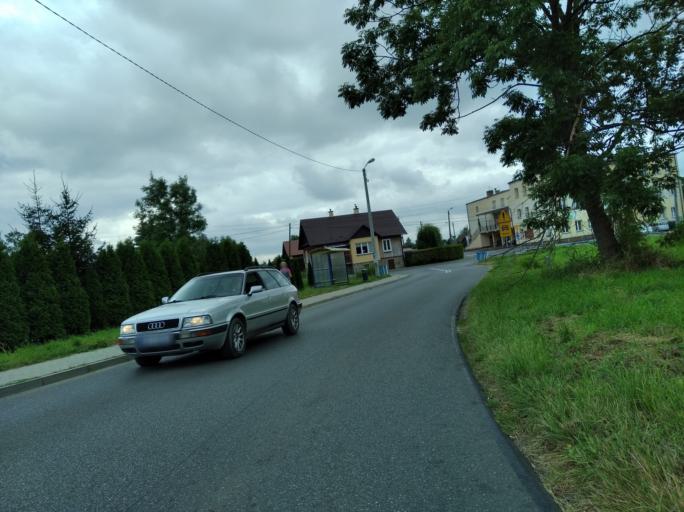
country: PL
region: Subcarpathian Voivodeship
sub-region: Powiat krosnienski
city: Odrzykon
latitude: 49.7397
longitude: 21.7399
